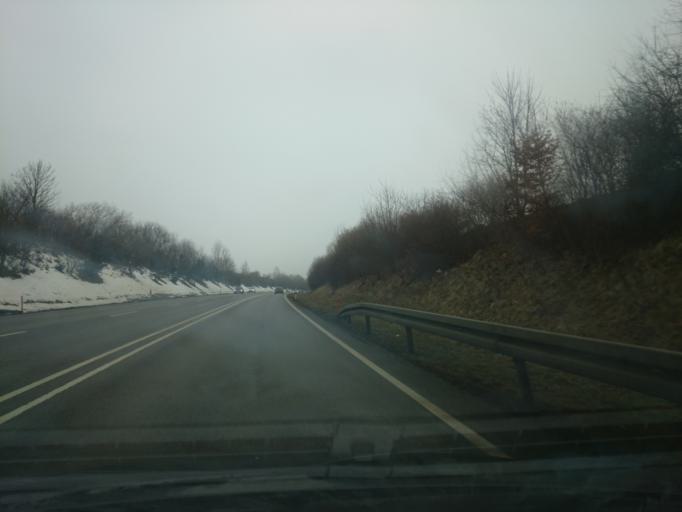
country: DE
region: Bavaria
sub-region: Swabia
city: Kuhbach
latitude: 48.4842
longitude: 11.1863
